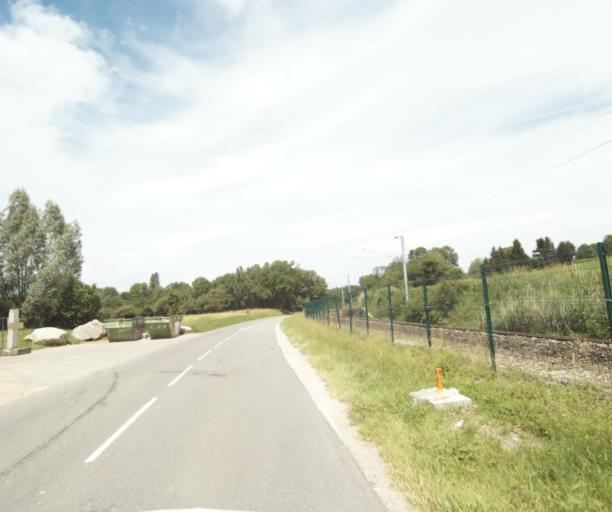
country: FR
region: Rhone-Alpes
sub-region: Departement de la Haute-Savoie
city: Margencel
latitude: 46.3276
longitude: 6.4377
